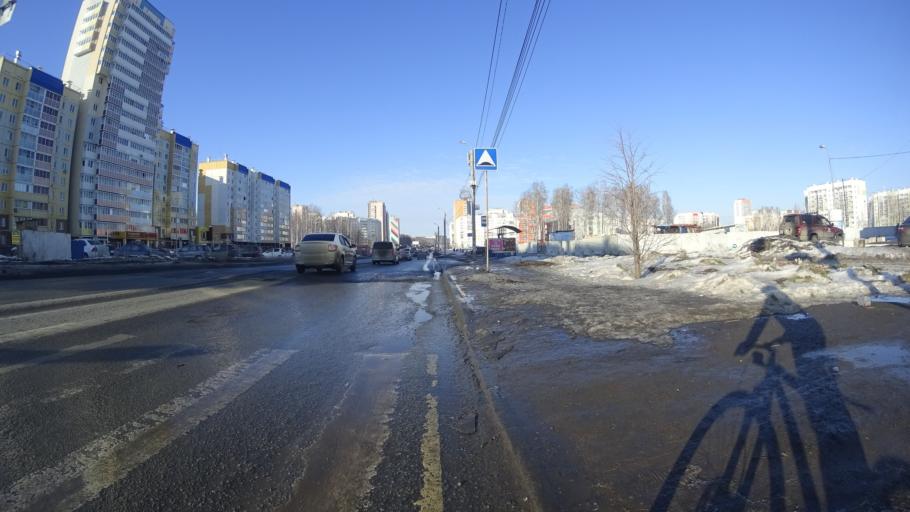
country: RU
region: Chelyabinsk
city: Roshchino
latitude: 55.2038
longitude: 61.2844
